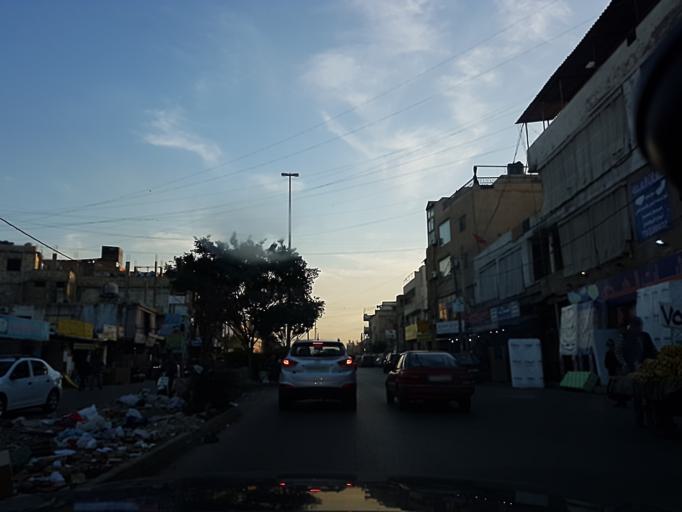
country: LB
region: Beyrouth
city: Beirut
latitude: 33.8478
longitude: 35.4851
